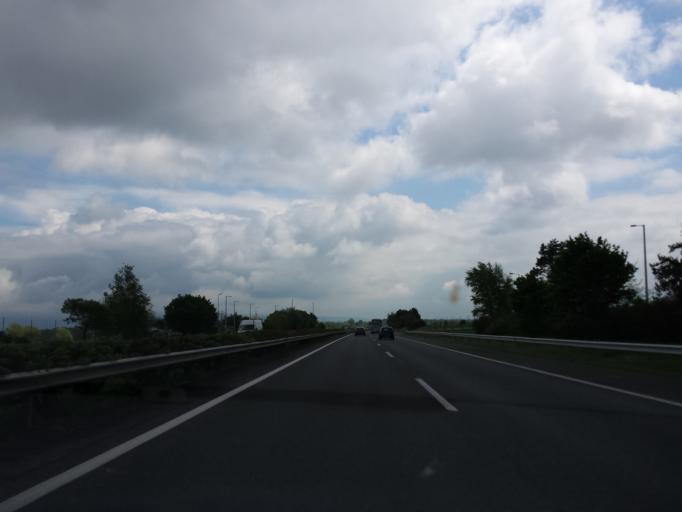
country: HU
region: Komarom-Esztergom
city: Kocs
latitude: 47.6353
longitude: 18.2405
